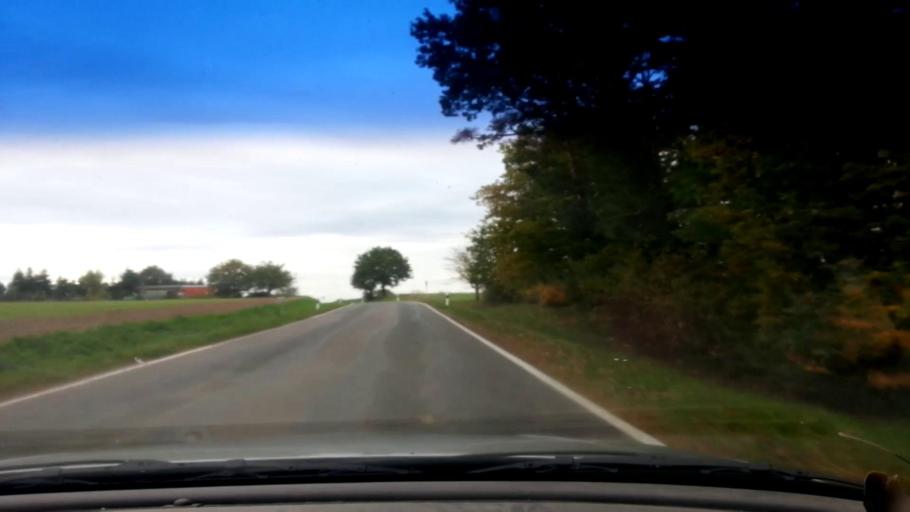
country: DE
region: Bavaria
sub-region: Upper Franconia
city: Priesendorf
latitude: 49.9152
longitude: 10.7143
